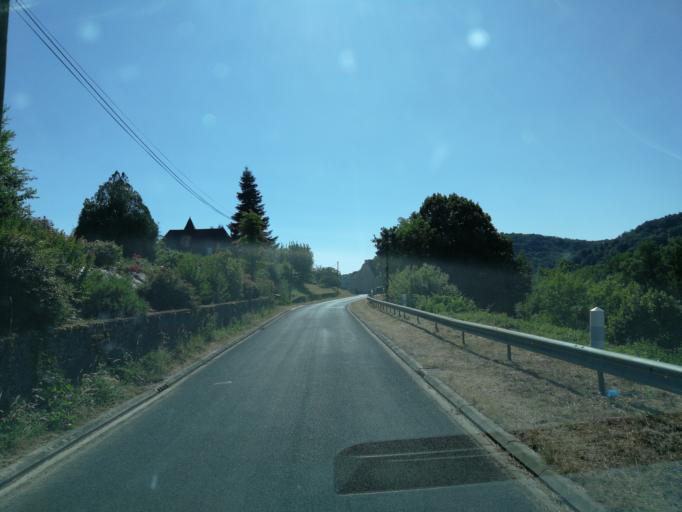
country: FR
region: Aquitaine
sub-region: Departement de la Dordogne
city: Eyvigues-et-Eybenes
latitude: 44.8663
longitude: 1.3731
